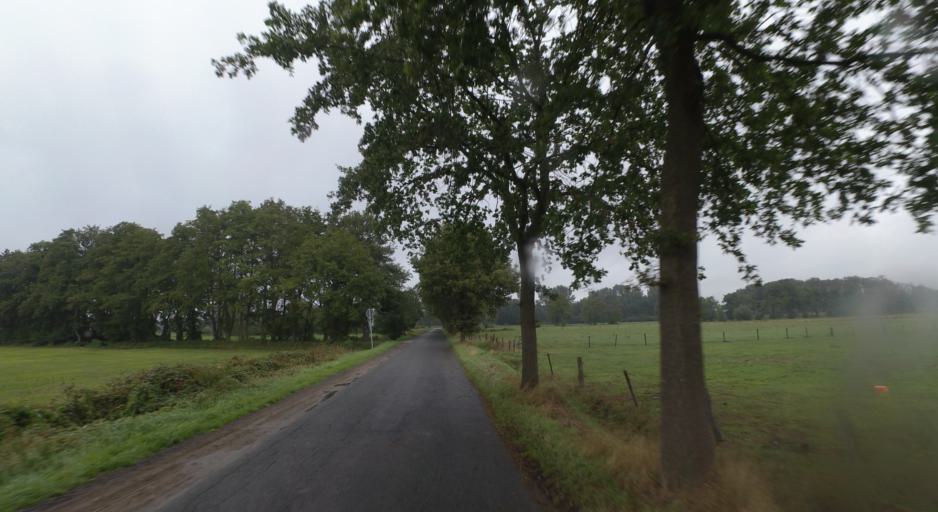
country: DE
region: North Rhine-Westphalia
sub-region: Regierungsbezirk Dusseldorf
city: Hamminkeln
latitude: 51.7199
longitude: 6.6108
